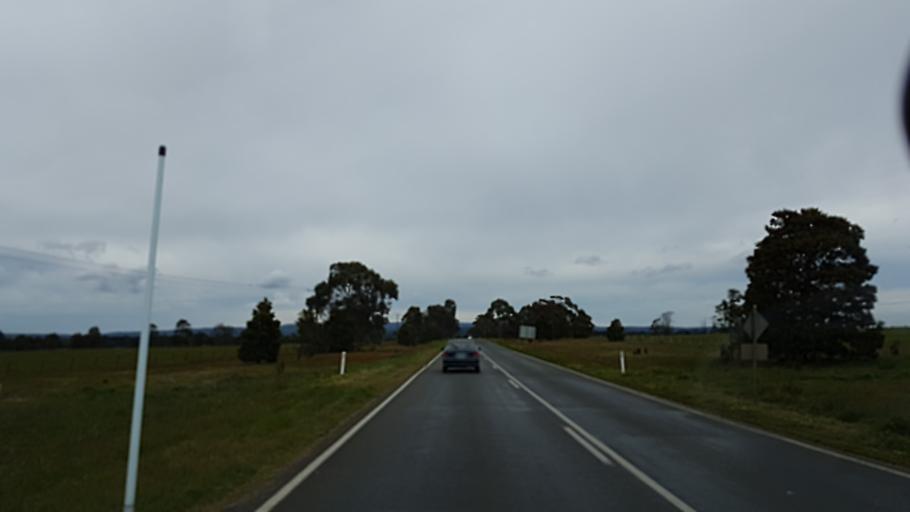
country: AU
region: Victoria
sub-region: Moorabool
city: Bacchus Marsh
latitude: -37.6222
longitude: 144.2108
